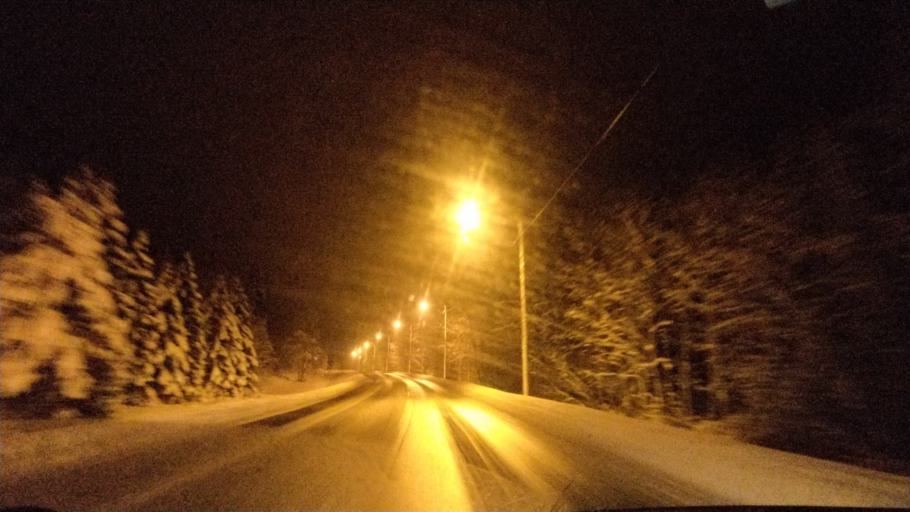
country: FI
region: Lapland
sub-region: Rovaniemi
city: Rovaniemi
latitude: 66.4026
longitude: 25.3899
